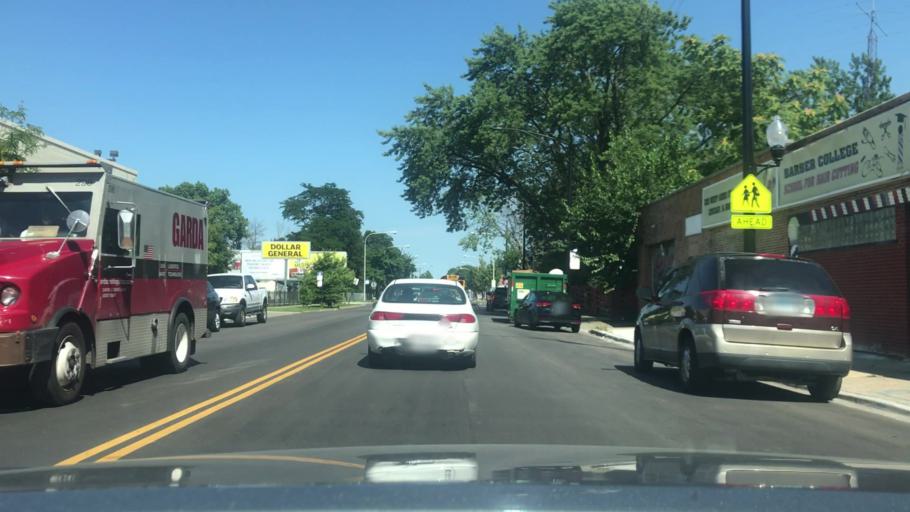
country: US
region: Illinois
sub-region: Cook County
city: Calumet Park
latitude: 41.7071
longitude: -87.6320
